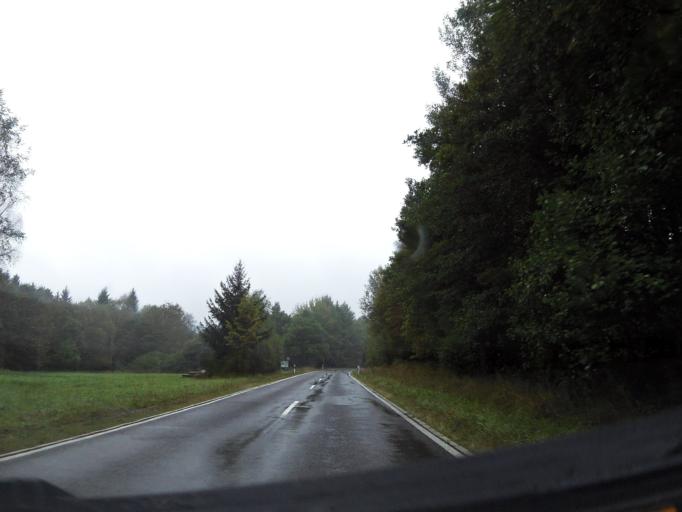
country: DE
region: Rheinland-Pfalz
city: Gebroth
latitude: 49.9330
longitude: 7.6421
